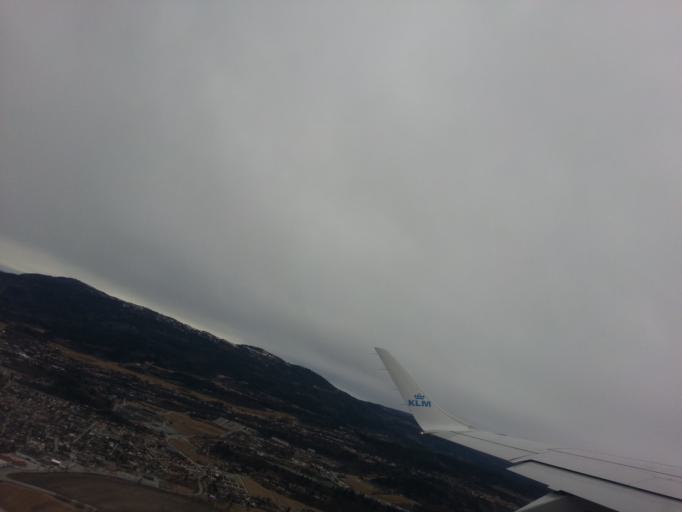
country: NO
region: Nord-Trondelag
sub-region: Stjordal
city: Stjordalshalsen
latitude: 63.4567
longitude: 10.9508
